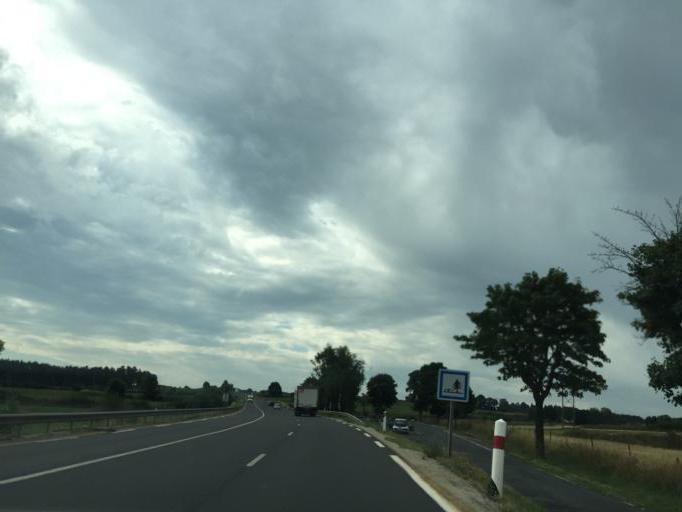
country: FR
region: Auvergne
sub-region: Departement de la Haute-Loire
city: Solignac-sur-Loire
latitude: 44.9181
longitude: 3.8448
